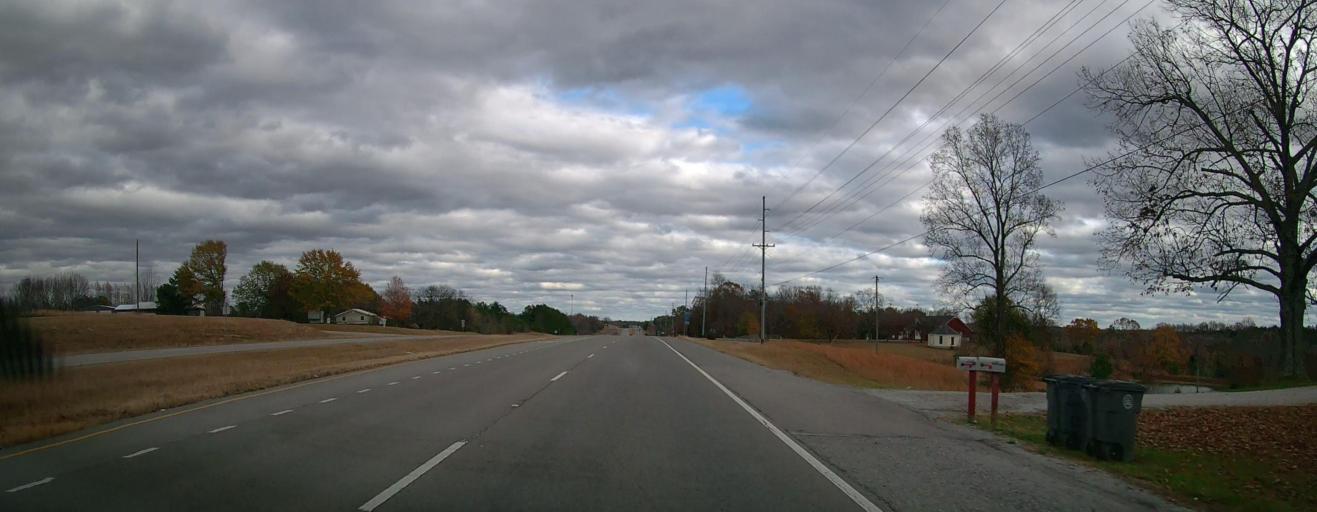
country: US
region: Alabama
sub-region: Lawrence County
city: Moulton
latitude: 34.5626
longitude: -87.3545
